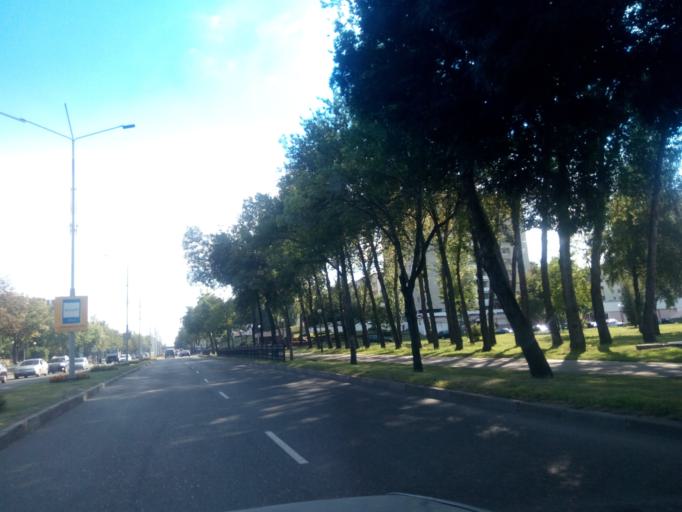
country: BY
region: Vitebsk
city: Navapolatsk
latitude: 55.5351
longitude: 28.6620
